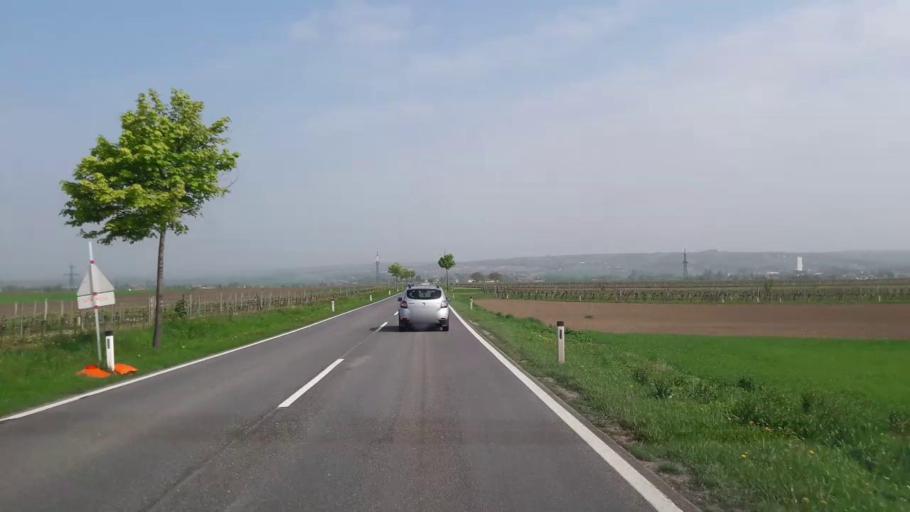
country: AT
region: Lower Austria
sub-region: Politischer Bezirk Hollabrunn
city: Haugsdorf
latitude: 48.6898
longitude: 16.0585
